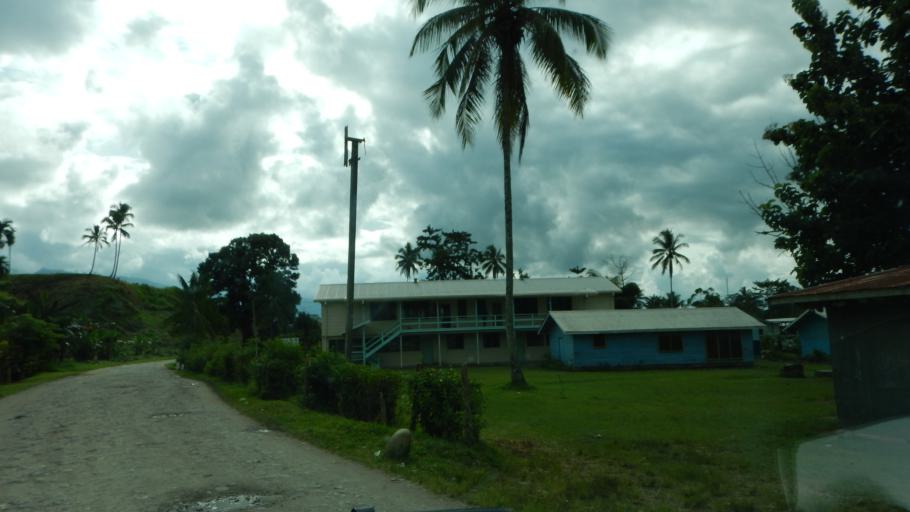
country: PG
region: Northern Province
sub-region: Sohe
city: Kokoda
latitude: -8.8775
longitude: 147.7388
